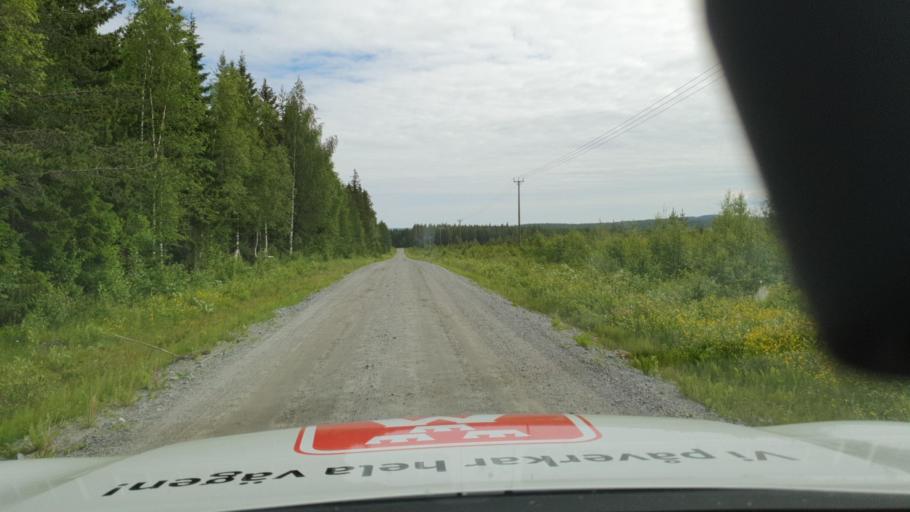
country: SE
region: Vaesterbotten
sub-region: Skelleftea Kommun
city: Langsele
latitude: 64.6471
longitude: 20.3150
